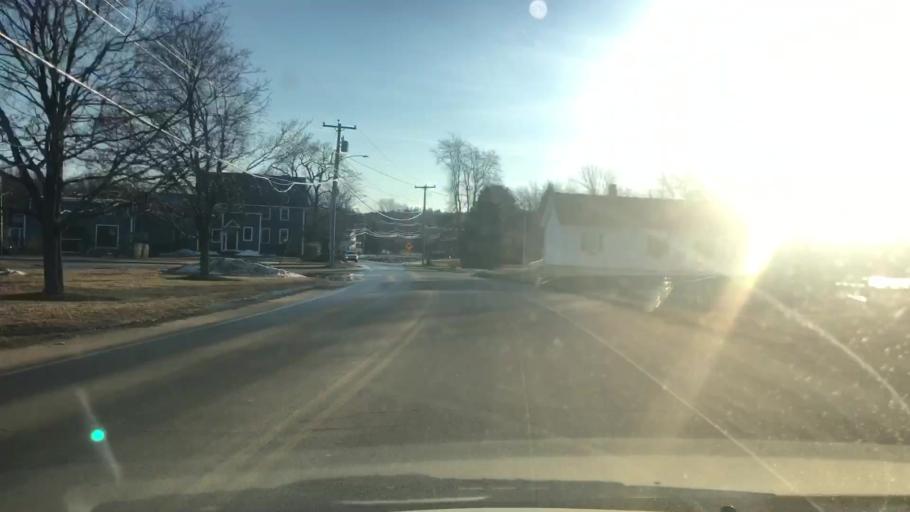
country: US
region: New Hampshire
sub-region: Hillsborough County
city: Milford
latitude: 42.8223
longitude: -71.6625
